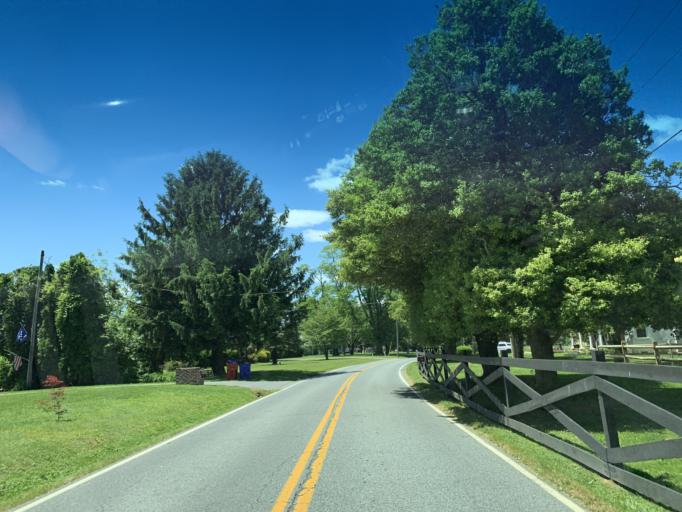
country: US
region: Maryland
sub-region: Cecil County
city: Rising Sun
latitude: 39.6975
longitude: -75.9862
